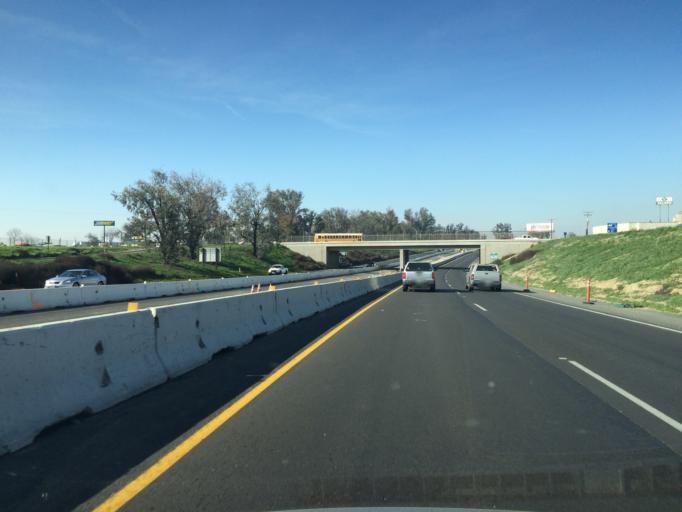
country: US
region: California
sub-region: Tulare County
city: Goshen
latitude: 36.3492
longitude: -119.4259
